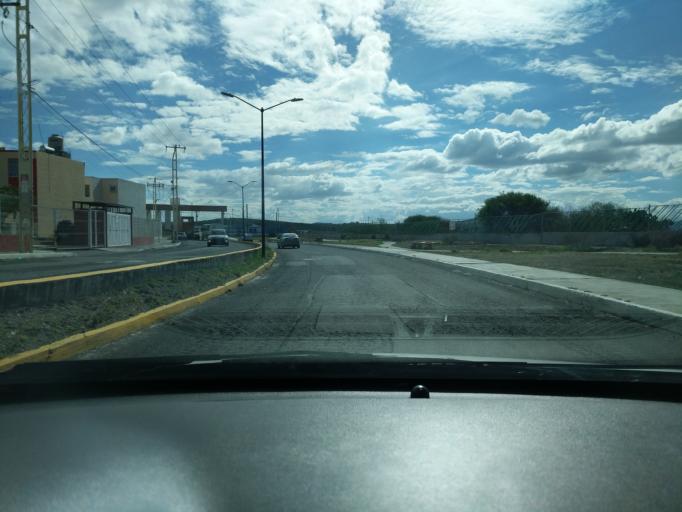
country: MX
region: Queretaro
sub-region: El Marques
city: Paseos del Marques
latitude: 20.6028
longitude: -100.2447
